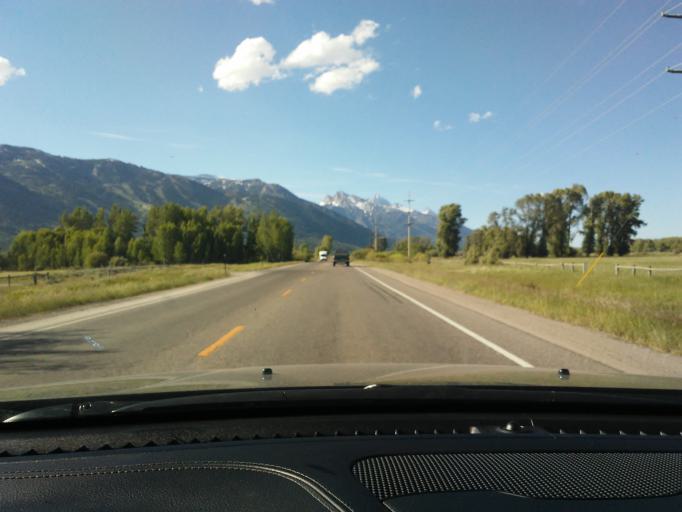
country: US
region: Wyoming
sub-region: Teton County
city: Moose Wilson Road
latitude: 43.5548
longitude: -110.8223
